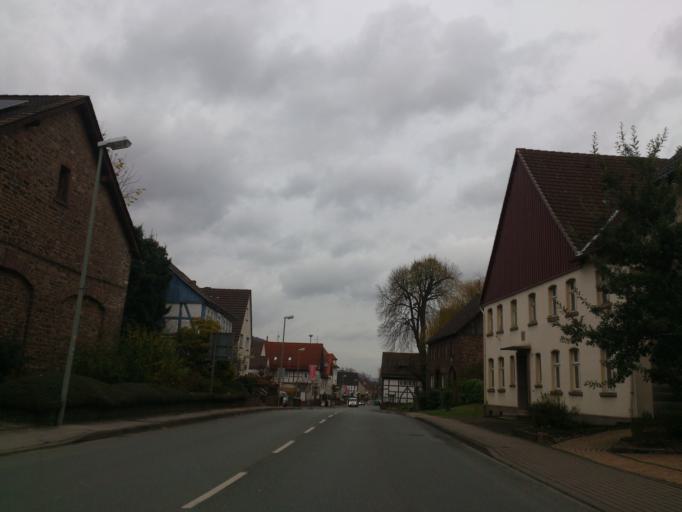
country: DE
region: Lower Saxony
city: Boffzen
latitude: 51.7345
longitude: 9.3625
